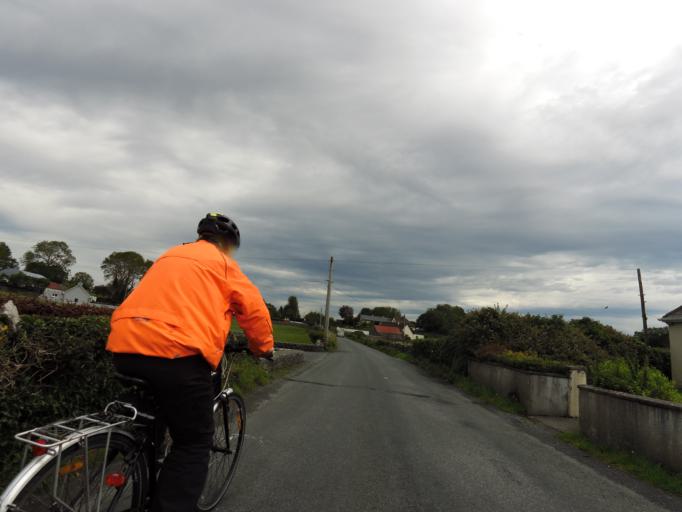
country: IE
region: Connaught
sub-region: County Galway
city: Gaillimh
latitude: 53.3149
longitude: -9.0361
